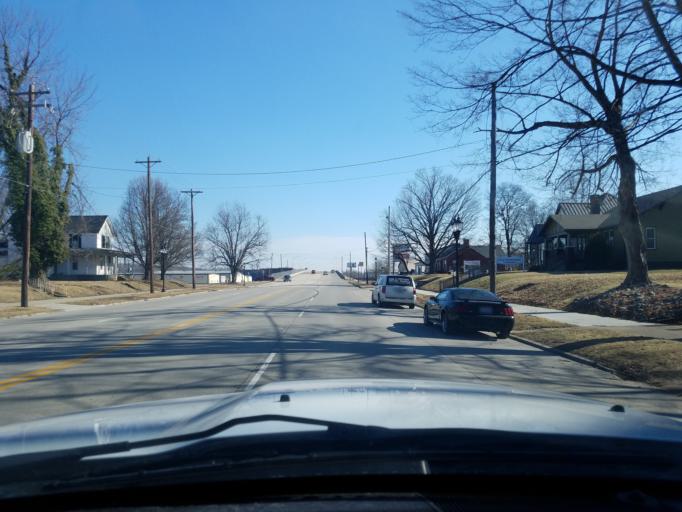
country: US
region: Kentucky
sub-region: Henderson County
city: Henderson
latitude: 37.8364
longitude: -87.5810
